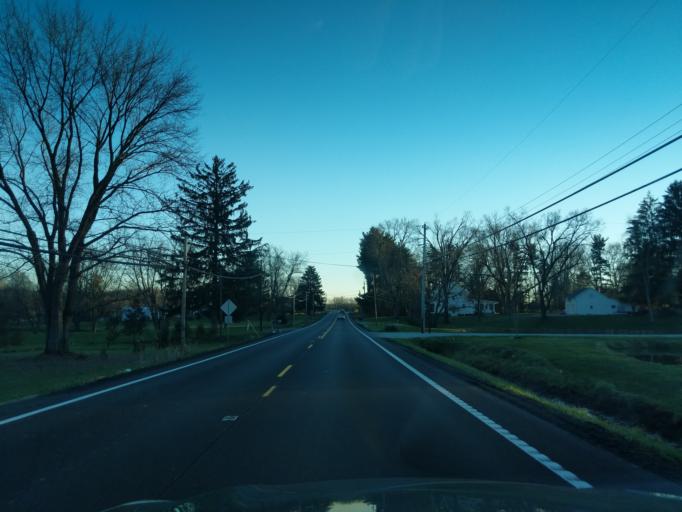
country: US
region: Ohio
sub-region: Licking County
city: Heath
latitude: 40.0037
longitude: -82.4049
